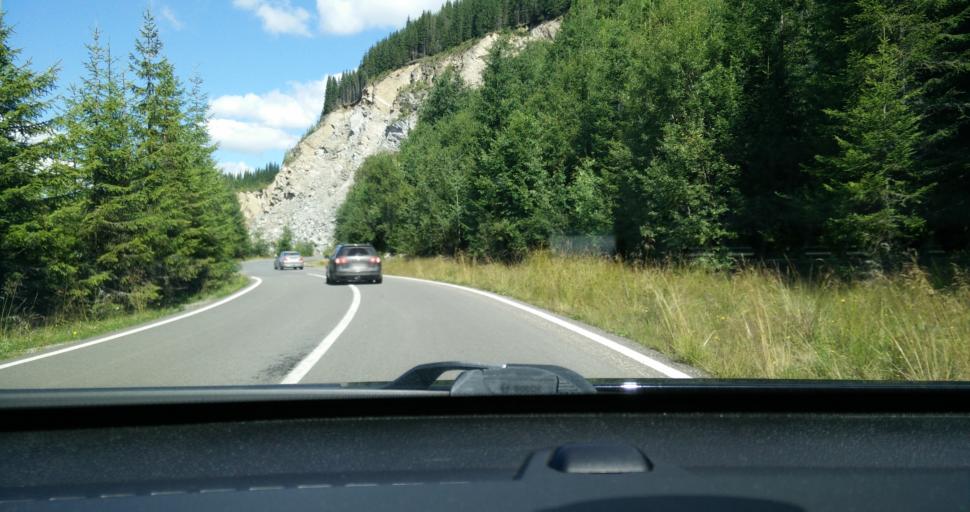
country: RO
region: Alba
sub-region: Comuna Sugag
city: Sugag
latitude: 45.5484
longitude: 23.6320
